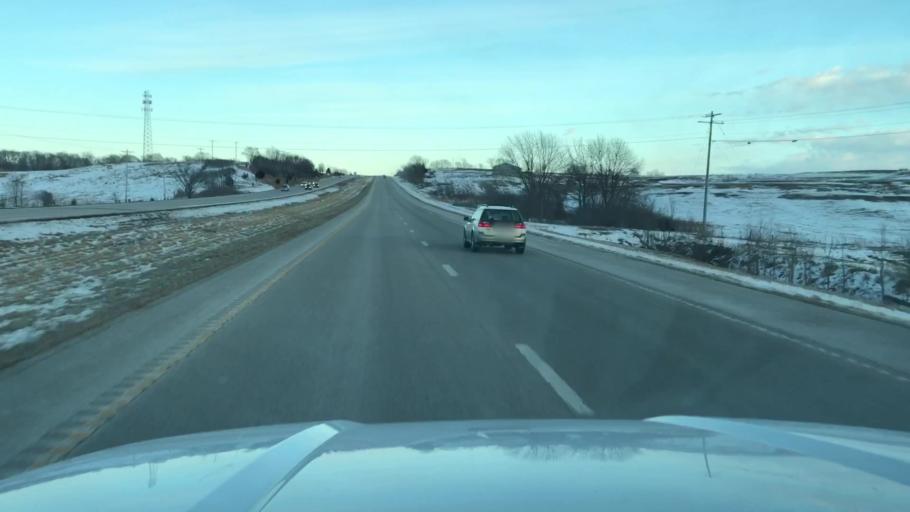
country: US
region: Missouri
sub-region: Clinton County
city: Gower
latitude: 39.7473
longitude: -94.6573
